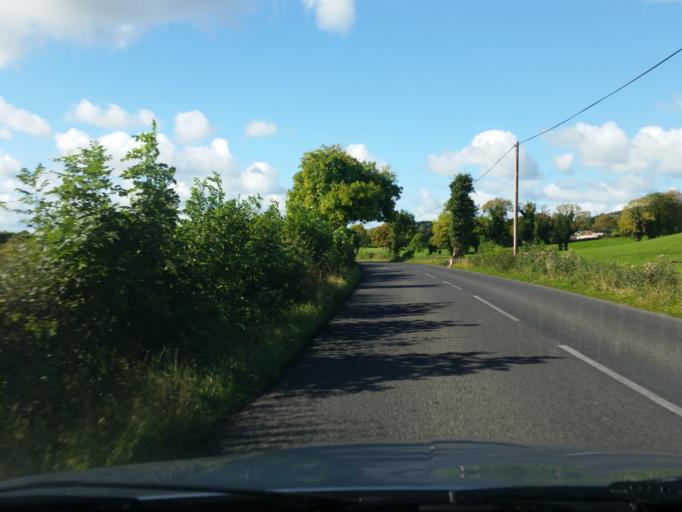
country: IE
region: Ulster
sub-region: County Monaghan
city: Clones
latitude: 54.2270
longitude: -7.3163
